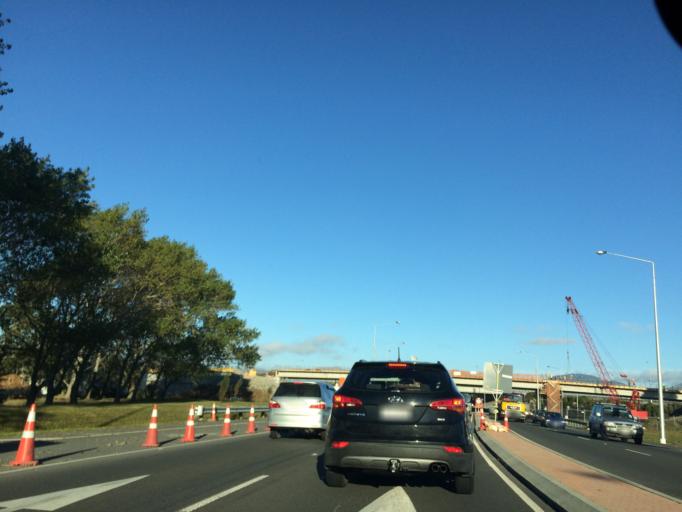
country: NZ
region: Canterbury
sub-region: Christchurch City
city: Christchurch
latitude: -43.5465
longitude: 172.5763
